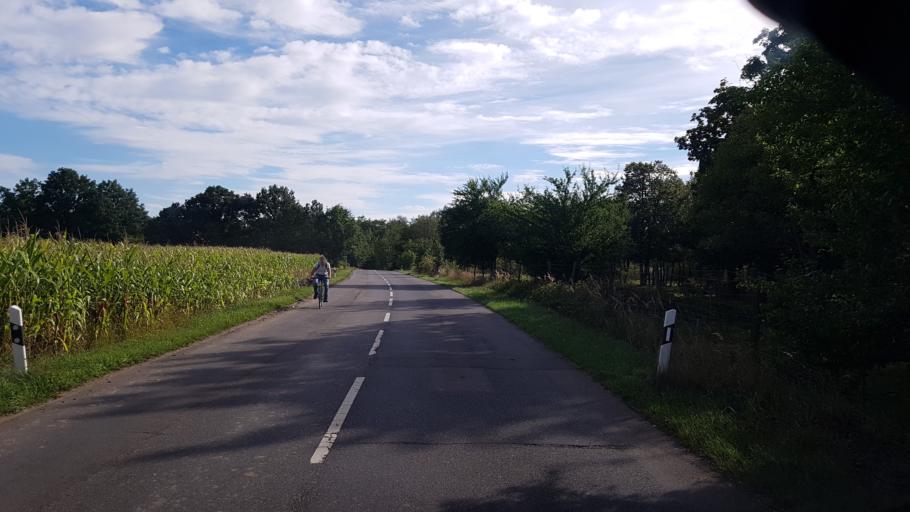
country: DE
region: Brandenburg
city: Spremberg
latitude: 51.5548
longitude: 14.3189
